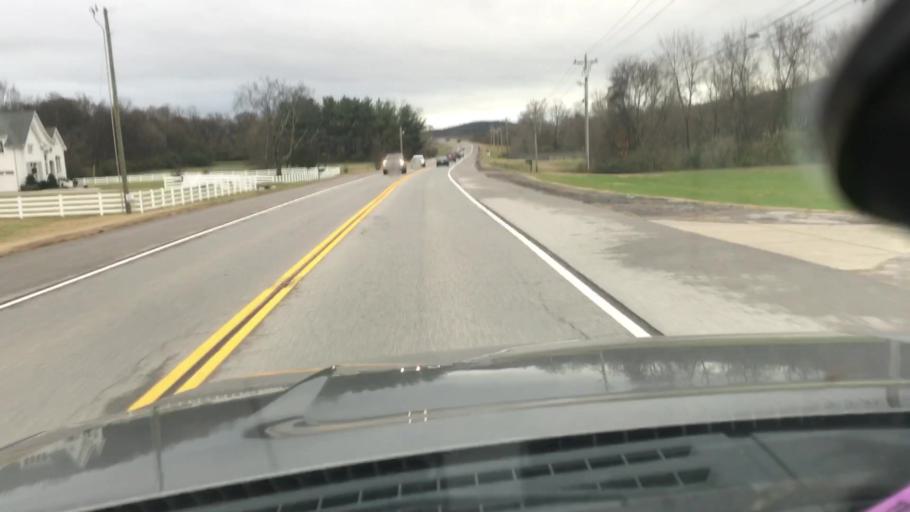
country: US
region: Tennessee
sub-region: Williamson County
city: Brentwood Estates
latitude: 35.9656
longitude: -86.7723
